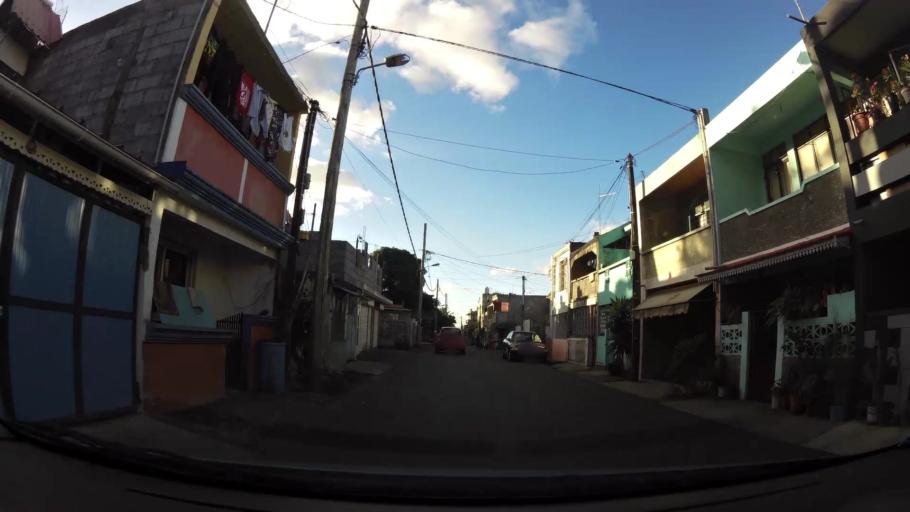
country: MU
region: Plaines Wilhems
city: Quatre Bornes
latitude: -20.2533
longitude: 57.4617
